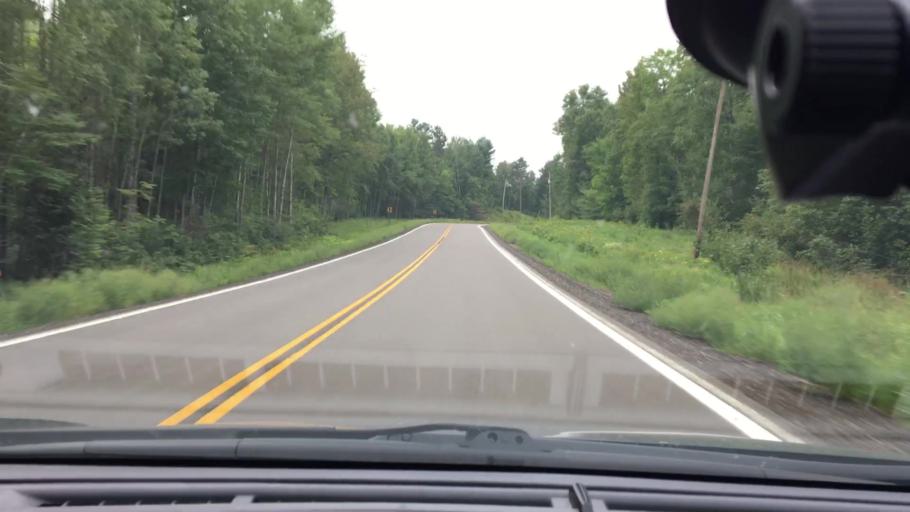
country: US
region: Minnesota
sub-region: Crow Wing County
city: Cross Lake
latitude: 46.6564
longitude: -93.9777
